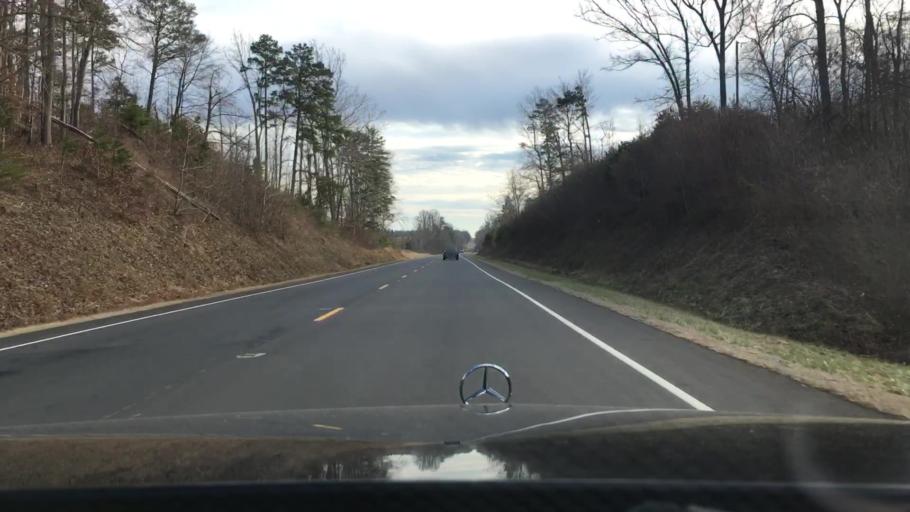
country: US
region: Virginia
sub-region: City of Danville
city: Danville
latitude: 36.5161
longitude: -79.3932
